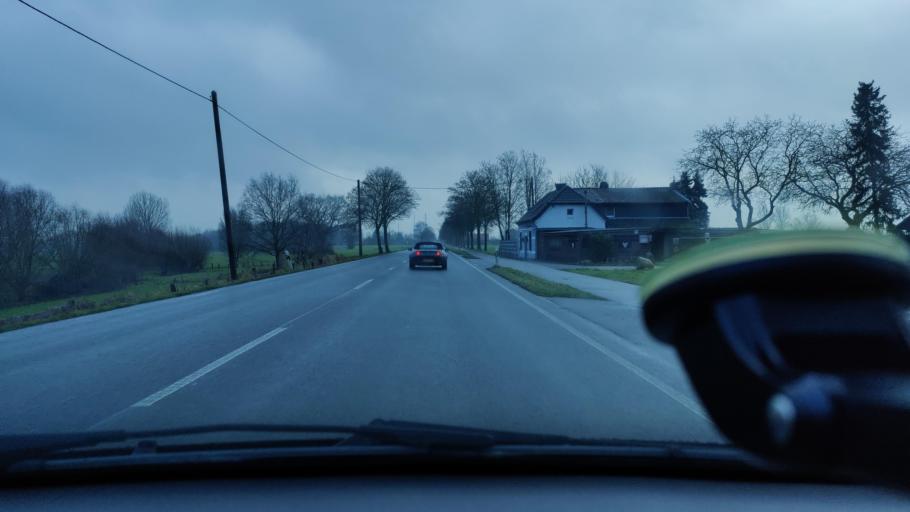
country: DE
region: North Rhine-Westphalia
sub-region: Regierungsbezirk Dusseldorf
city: Alpen
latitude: 51.5806
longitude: 6.5552
